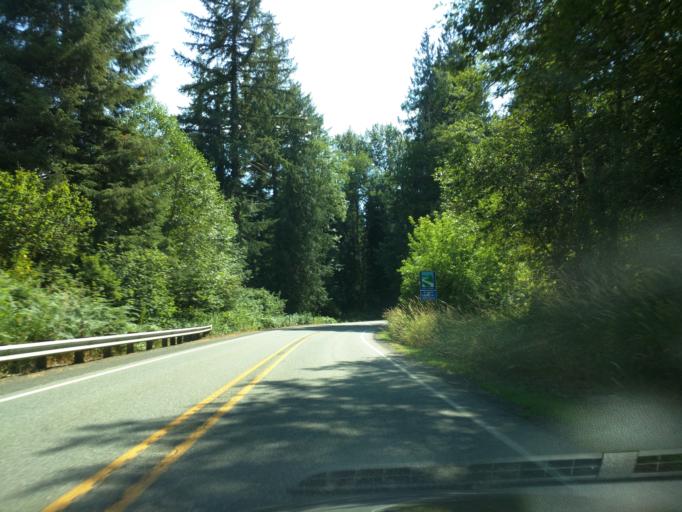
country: US
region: Washington
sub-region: Whatcom County
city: Peaceful Valley
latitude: 48.9220
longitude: -122.0543
